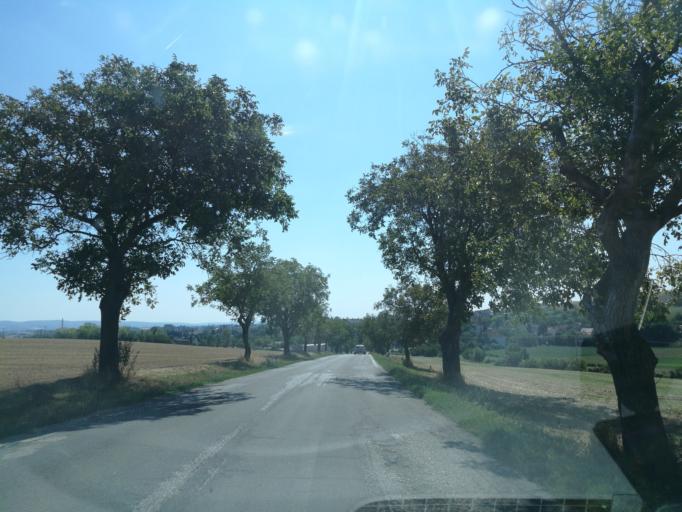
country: SK
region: Trnavsky
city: Vrbove
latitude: 48.6330
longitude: 17.7200
